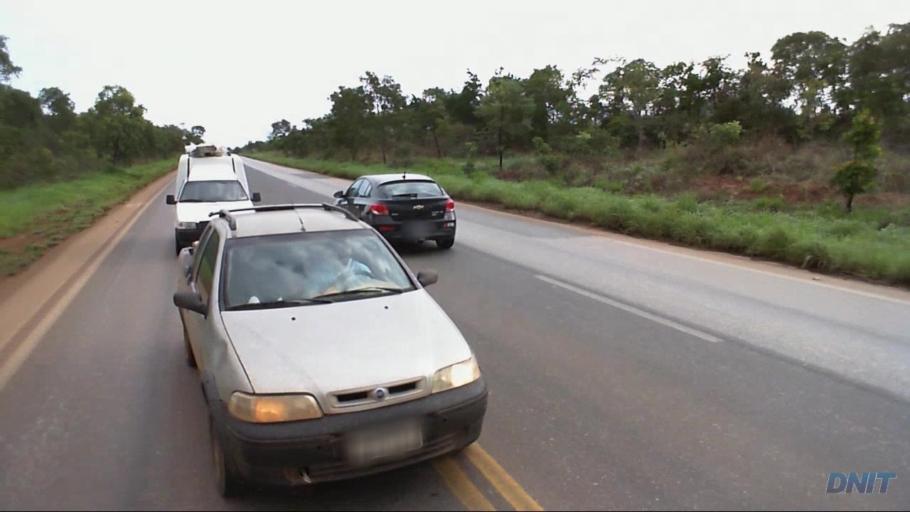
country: BR
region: Goias
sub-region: Uruacu
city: Uruacu
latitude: -14.5777
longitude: -49.1587
